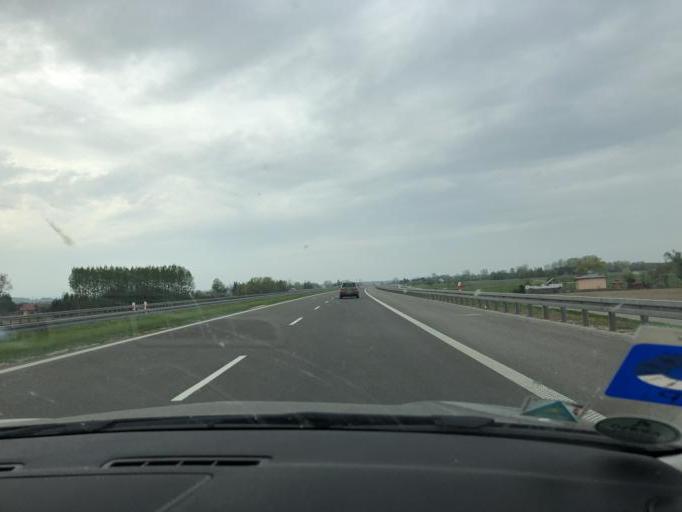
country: PL
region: Subcarpathian Voivodeship
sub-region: Powiat lancucki
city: Gluchow
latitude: 50.1039
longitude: 22.2800
